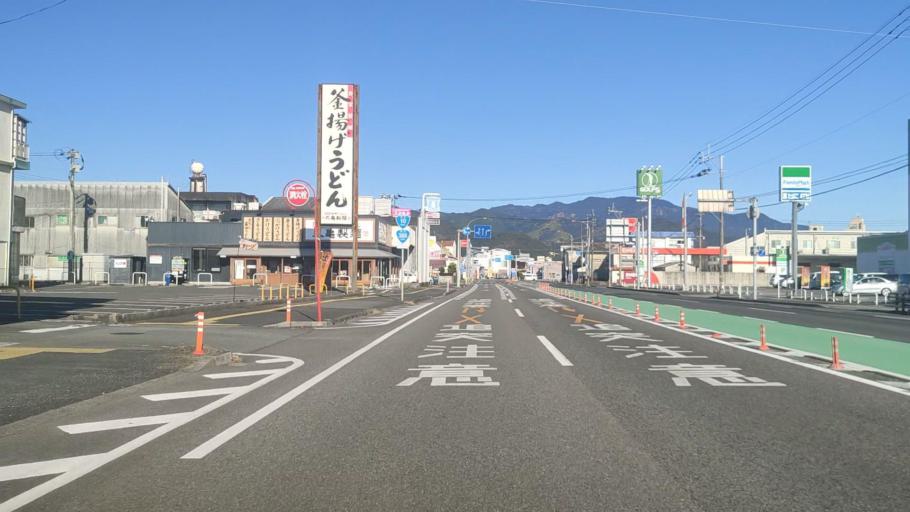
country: JP
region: Miyazaki
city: Nobeoka
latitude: 32.5877
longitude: 131.6767
